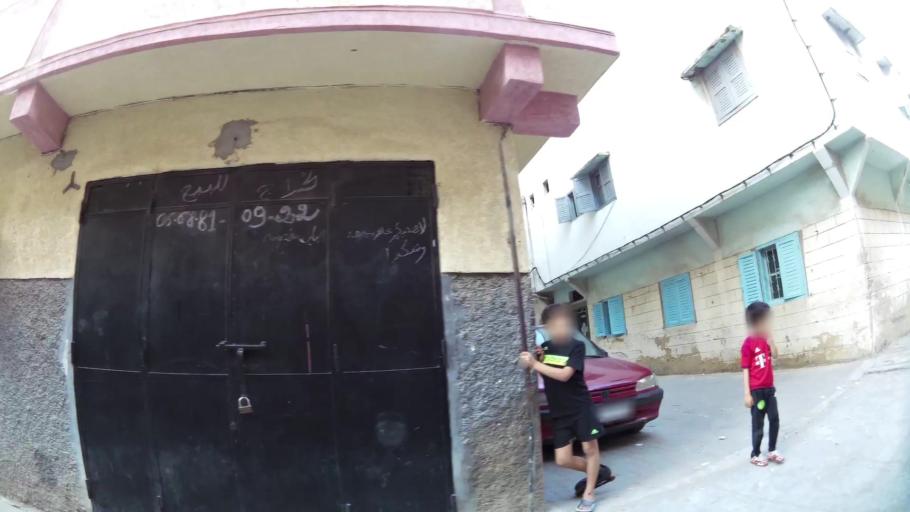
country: MA
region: Rabat-Sale-Zemmour-Zaer
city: Sale
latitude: 34.0538
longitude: -6.7740
